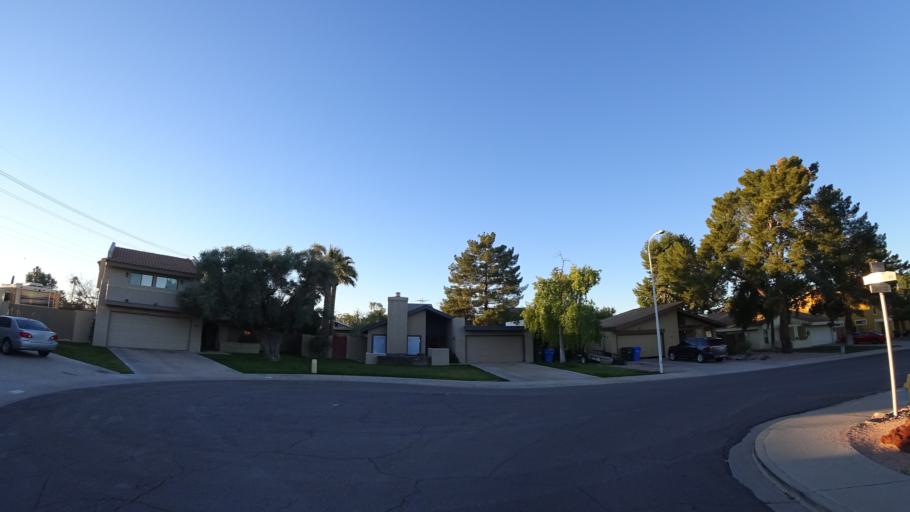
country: US
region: Arizona
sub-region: Maricopa County
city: Paradise Valley
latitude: 33.4771
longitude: -111.9616
